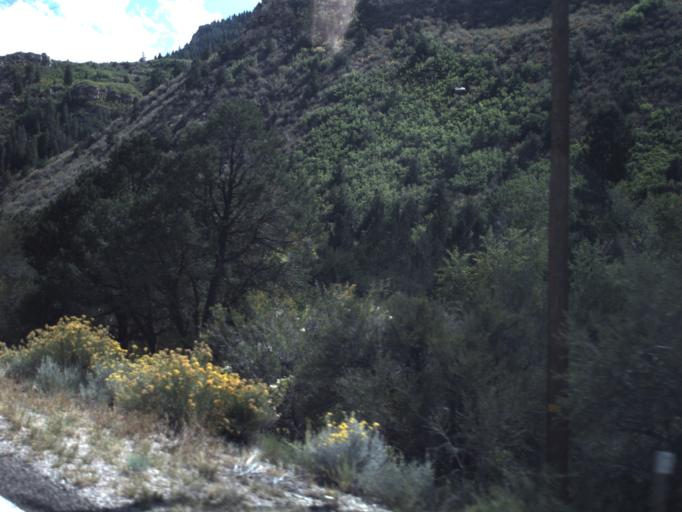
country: US
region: Utah
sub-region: Iron County
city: Cedar City
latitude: 37.6470
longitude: -112.9707
